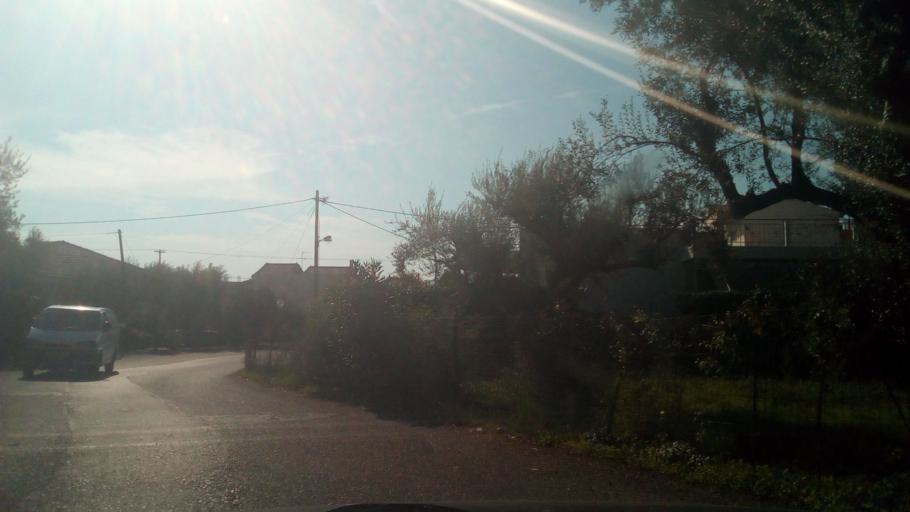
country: GR
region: West Greece
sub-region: Nomos Aitolias kai Akarnanias
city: Nafpaktos
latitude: 38.4026
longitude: 21.8556
